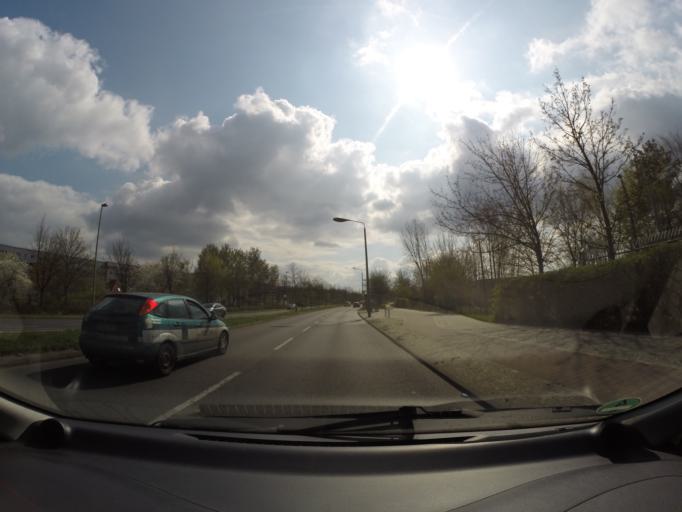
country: DE
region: Berlin
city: Kaulsdorf
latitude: 52.5340
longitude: 13.5877
